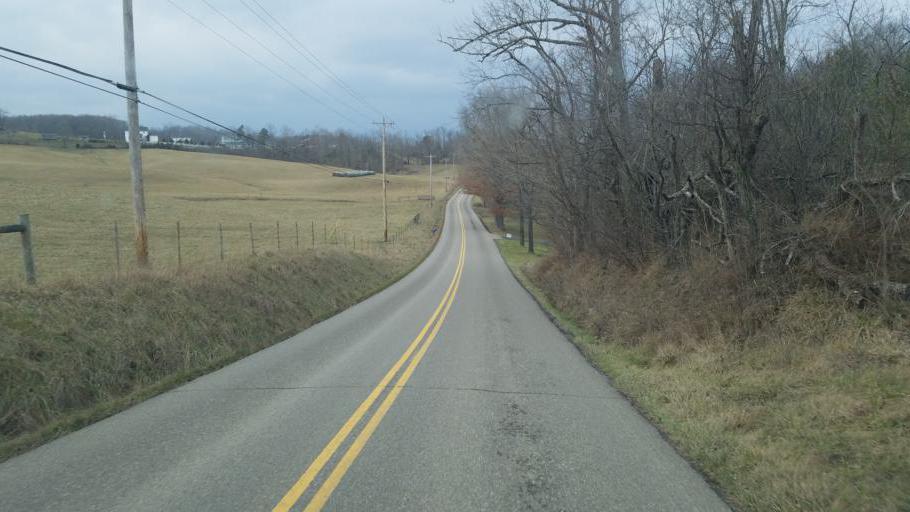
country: US
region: Ohio
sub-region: Gallia County
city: Gallipolis
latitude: 38.7656
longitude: -82.3742
